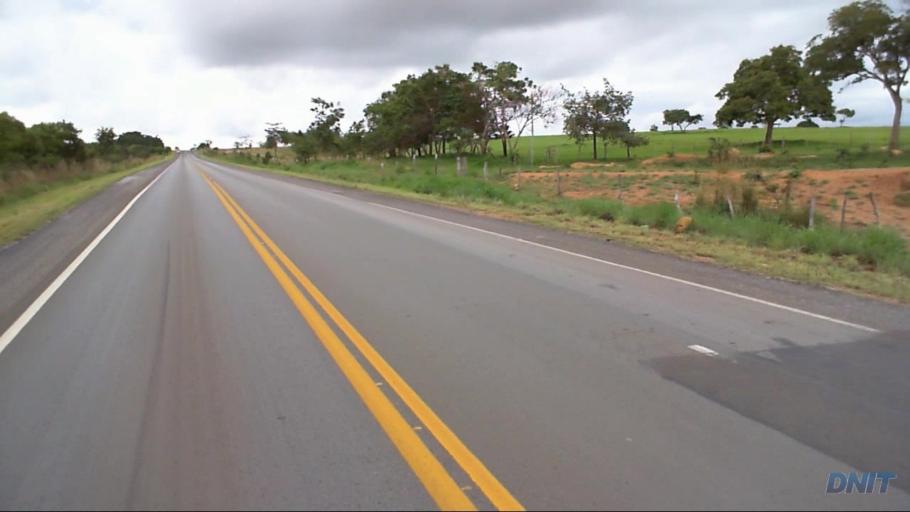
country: BR
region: Goias
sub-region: Padre Bernardo
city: Padre Bernardo
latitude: -15.2151
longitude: -48.5942
